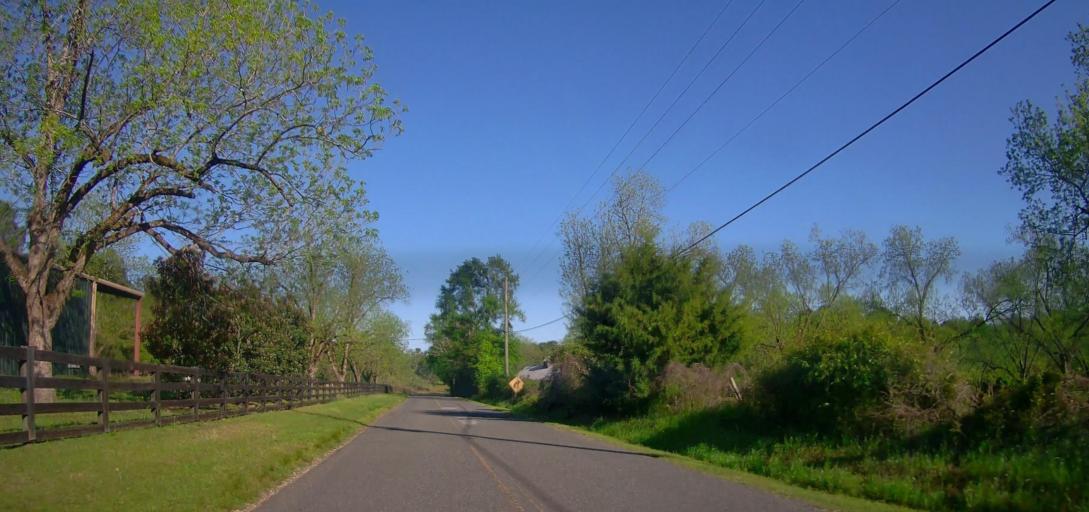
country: US
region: Georgia
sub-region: Houston County
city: Perry
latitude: 32.4811
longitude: -83.7990
